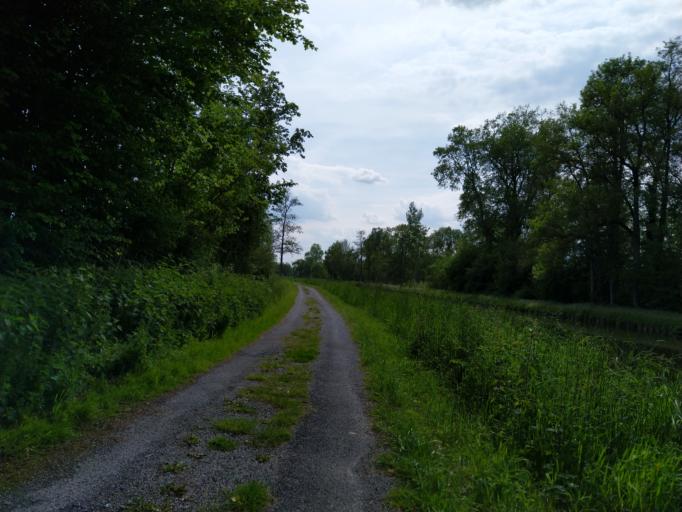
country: FR
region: Picardie
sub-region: Departement de l'Aisne
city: Etreux
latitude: 49.9780
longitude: 3.6343
